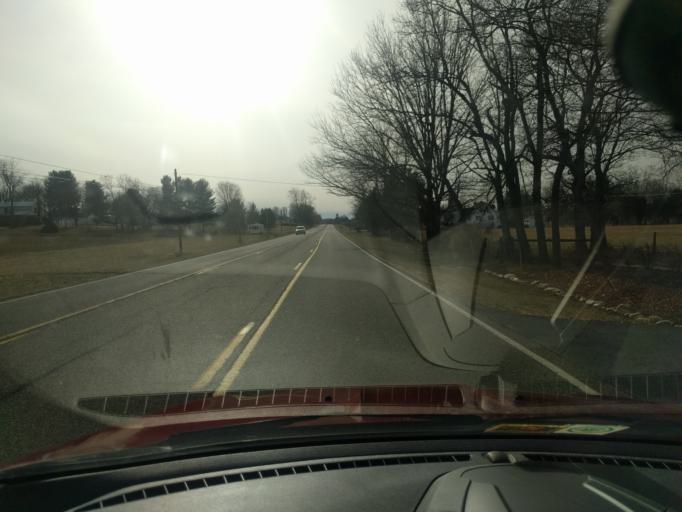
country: US
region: Virginia
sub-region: Augusta County
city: Stuarts Draft
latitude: 37.9889
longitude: -79.1633
